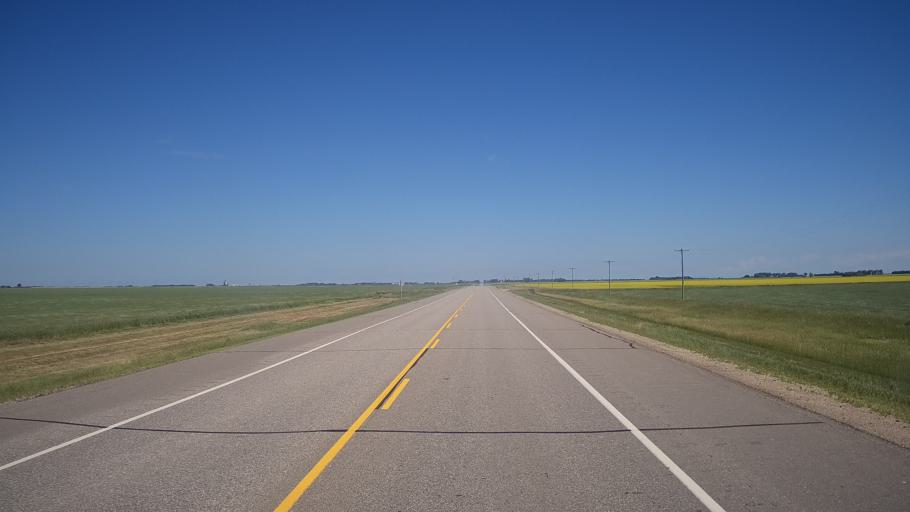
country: CA
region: Manitoba
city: Portage la Prairie
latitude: 50.0097
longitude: -98.4688
